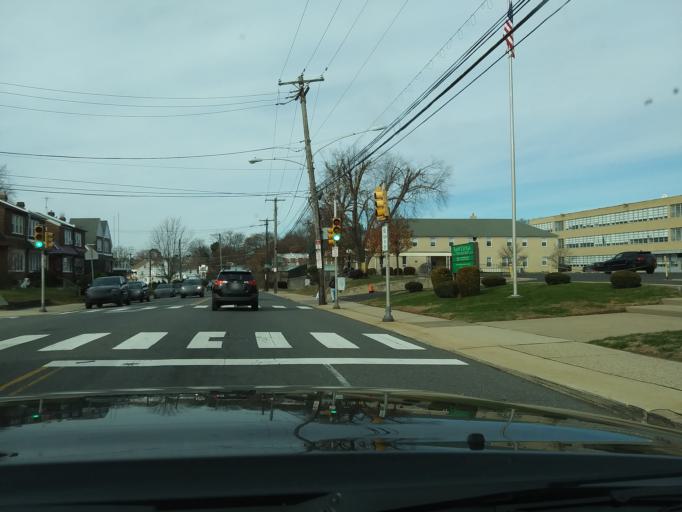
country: US
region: Pennsylvania
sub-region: Montgomery County
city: Rockledge
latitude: 40.0759
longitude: -75.0807
